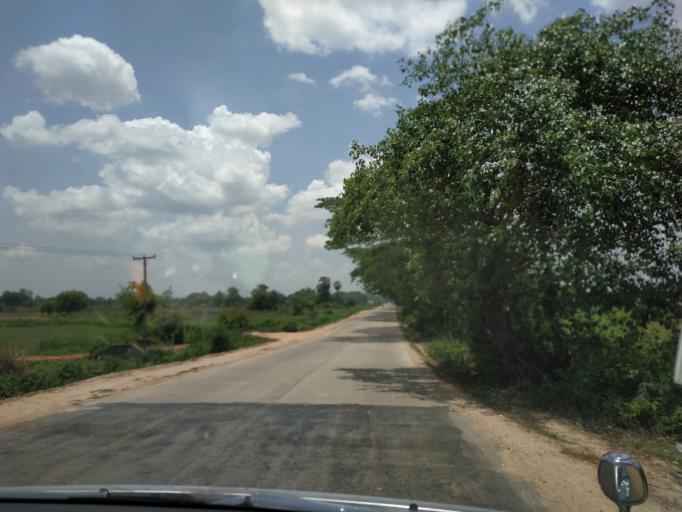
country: MM
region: Bago
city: Bago
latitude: 17.4776
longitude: 96.5029
